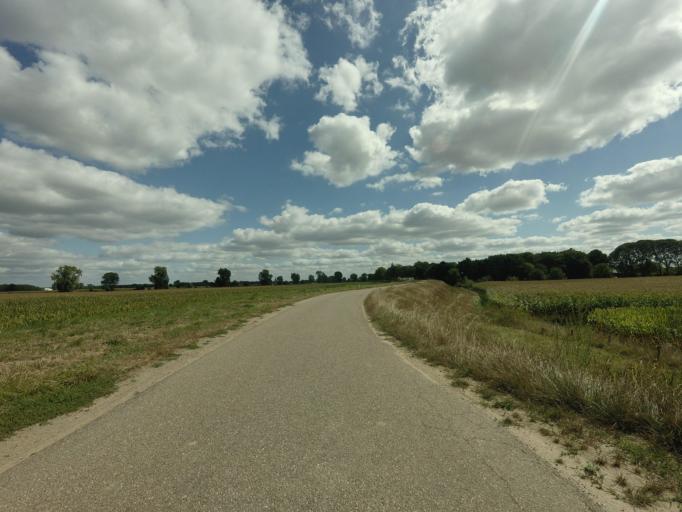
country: NL
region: North Brabant
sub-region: Gemeente Oss
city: Berghem
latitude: 51.8219
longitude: 5.6032
